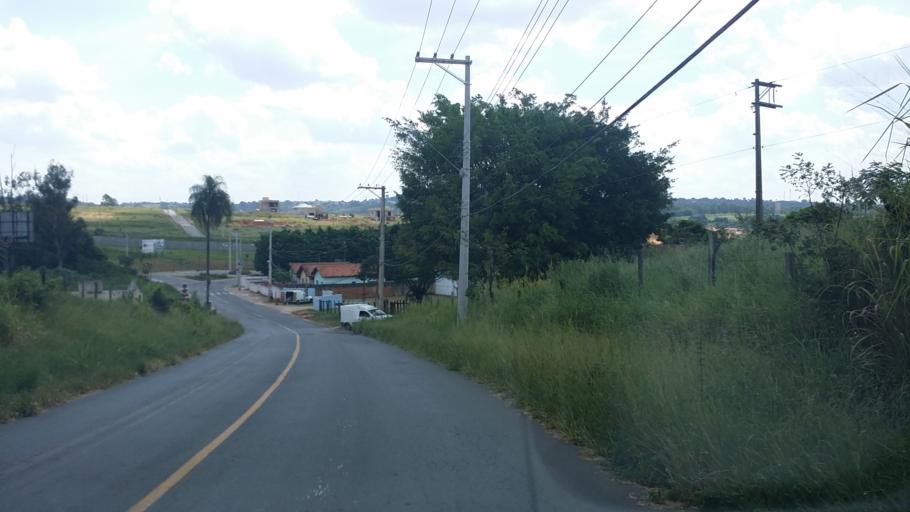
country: BR
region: Sao Paulo
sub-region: Itupeva
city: Itupeva
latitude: -23.1782
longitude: -47.0464
